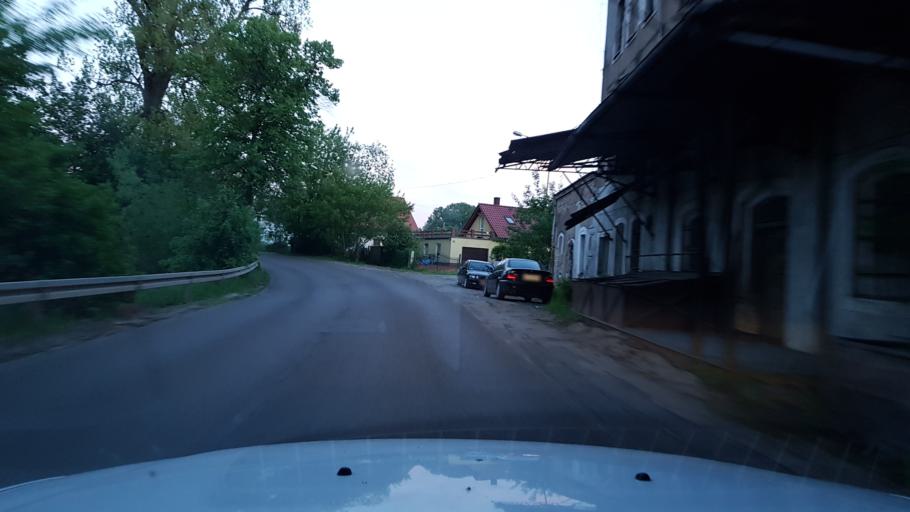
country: PL
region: West Pomeranian Voivodeship
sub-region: Powiat goleniowski
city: Goleniow
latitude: 53.5535
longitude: 14.8533
